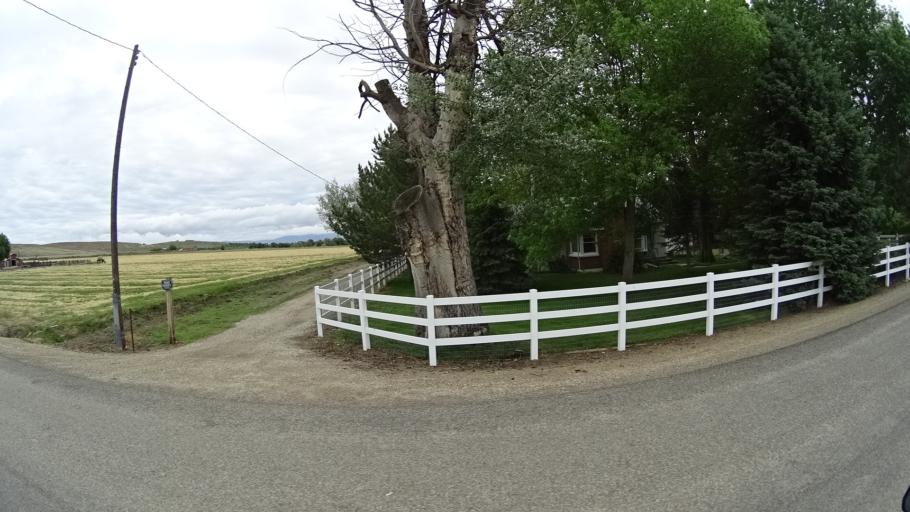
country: US
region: Idaho
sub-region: Ada County
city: Eagle
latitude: 43.7316
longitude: -116.4134
